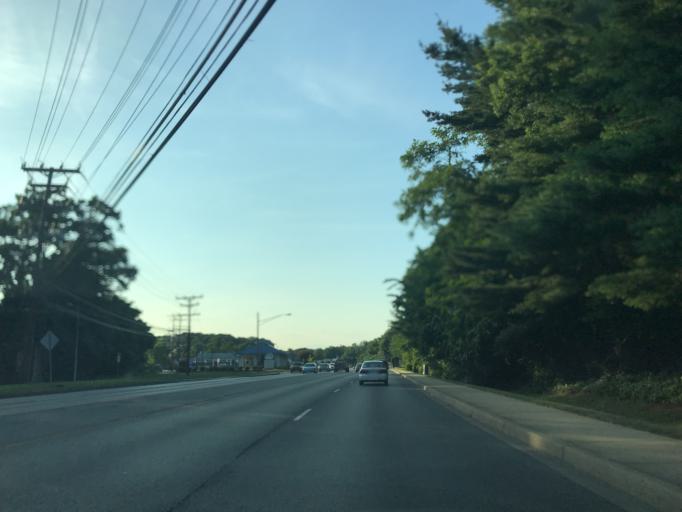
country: US
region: Maryland
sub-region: Anne Arundel County
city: Robinwood
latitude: 38.9592
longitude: -76.5097
